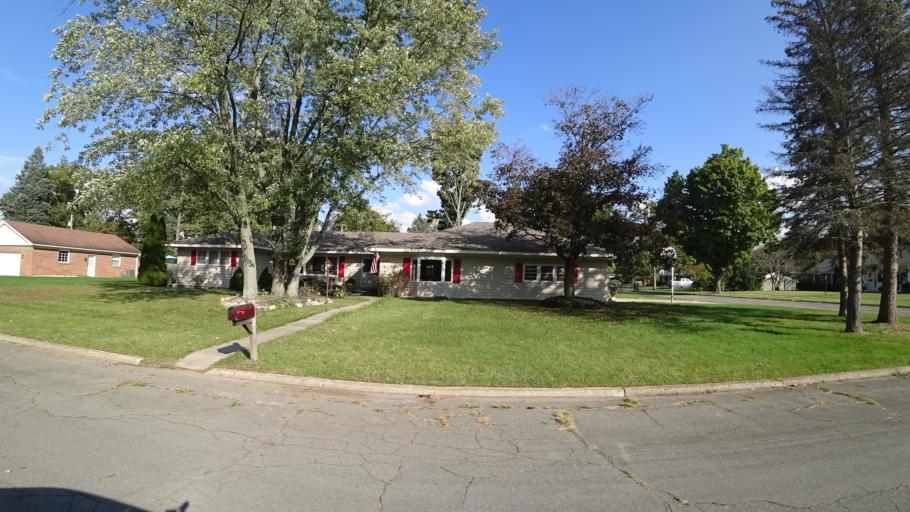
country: US
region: Michigan
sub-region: Saint Joseph County
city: Three Rivers
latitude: 41.9576
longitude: -85.6333
